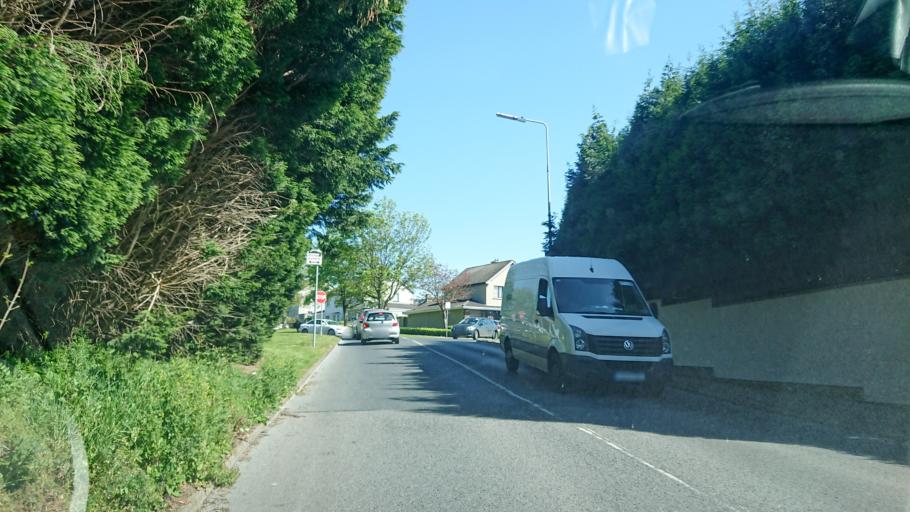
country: IE
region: Munster
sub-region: Waterford
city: Waterford
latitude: 52.2537
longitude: -7.1449
